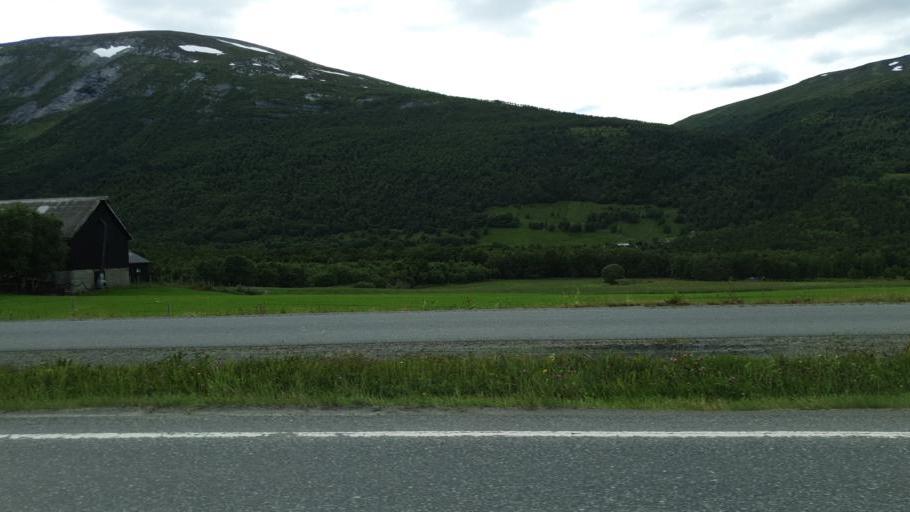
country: NO
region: Sor-Trondelag
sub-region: Oppdal
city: Oppdal
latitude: 62.5263
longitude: 9.6098
